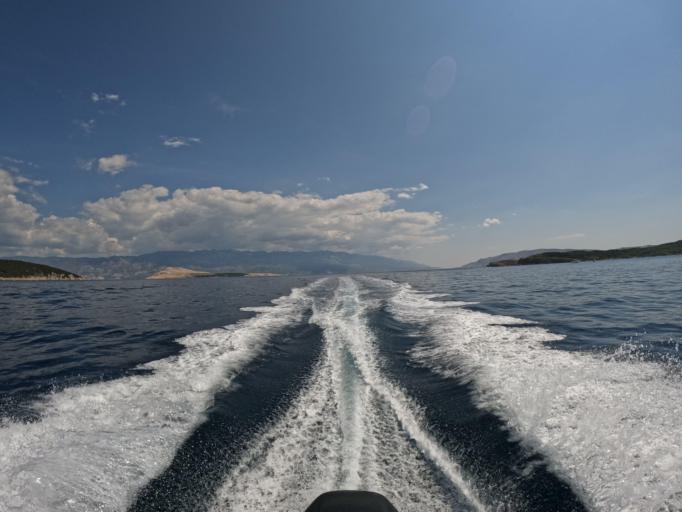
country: HR
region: Primorsko-Goranska
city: Lopar
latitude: 44.8524
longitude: 14.7554
